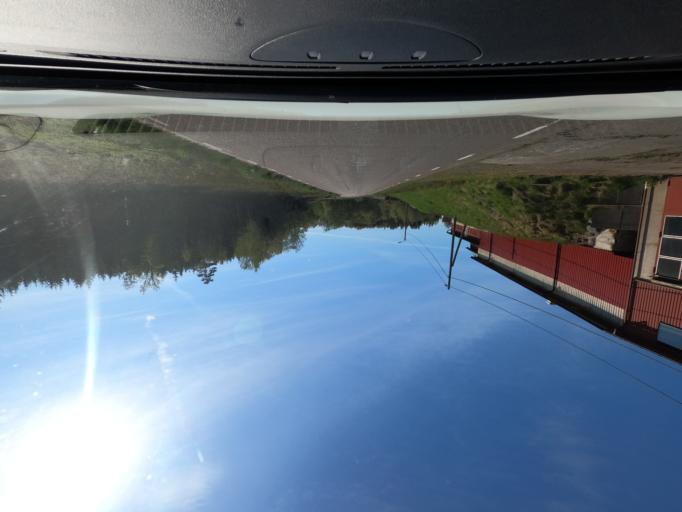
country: SE
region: Vaestra Goetaland
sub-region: Harryda Kommun
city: Landvetter
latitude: 57.6189
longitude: 12.3022
